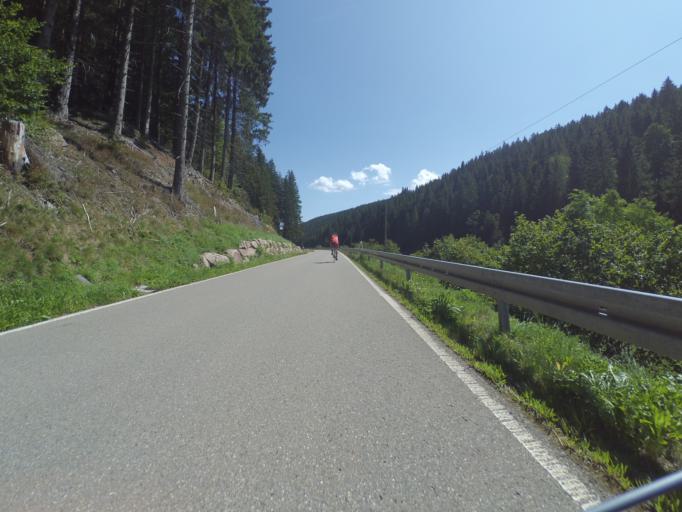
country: DE
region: Baden-Wuerttemberg
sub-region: Freiburg Region
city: Vohrenbach
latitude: 48.0217
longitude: 8.2796
